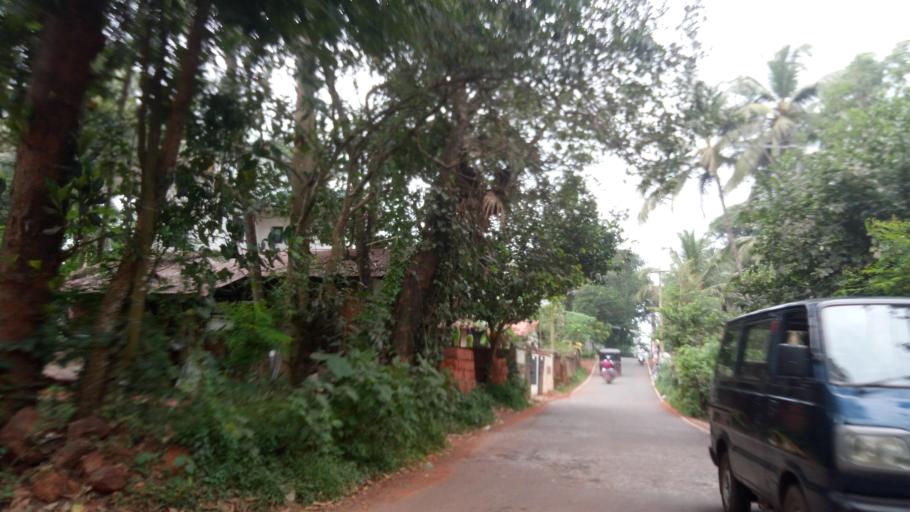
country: IN
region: Kerala
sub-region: Malappuram
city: Malappuram
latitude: 10.9865
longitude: 76.0072
